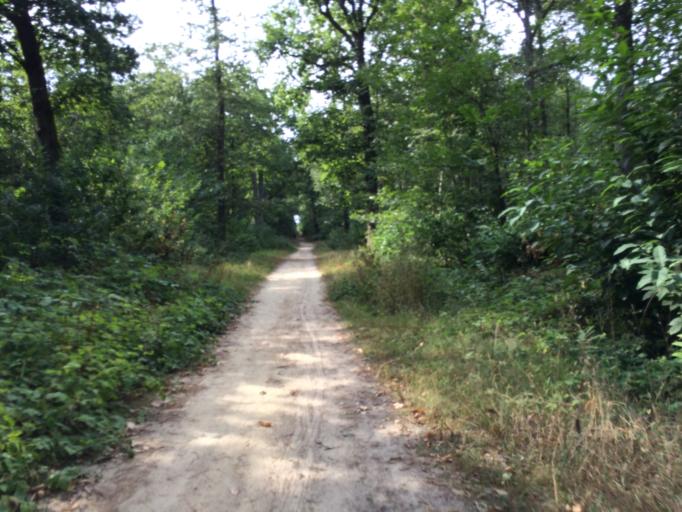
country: FR
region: Ile-de-France
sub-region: Departement de l'Essonne
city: Epinay-sous-Senart
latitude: 48.6822
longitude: 2.5075
